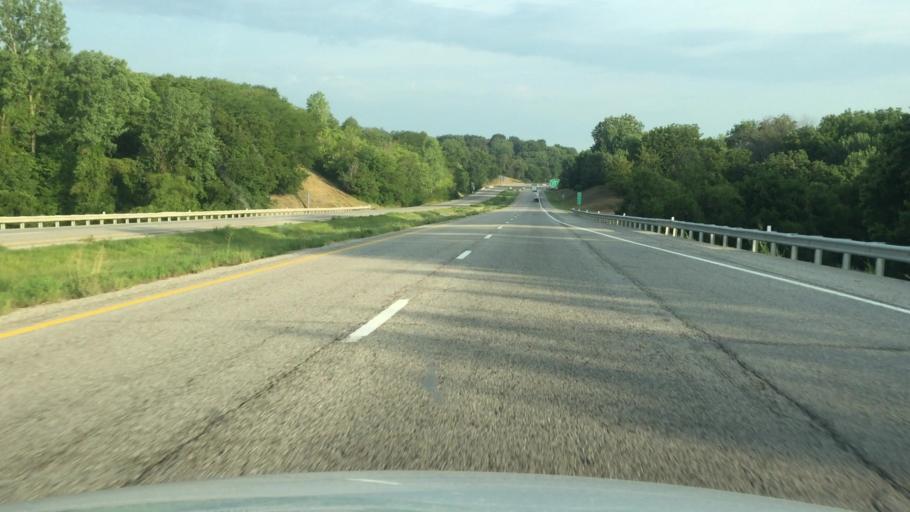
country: US
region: Missouri
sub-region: Buchanan County
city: Saint Joseph
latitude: 39.7245
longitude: -94.8387
